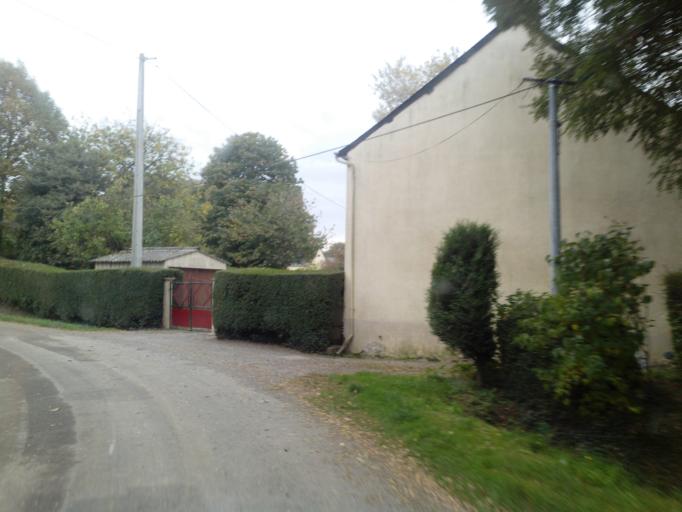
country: FR
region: Brittany
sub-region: Departement du Morbihan
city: Meneac
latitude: 48.1190
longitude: -2.4085
